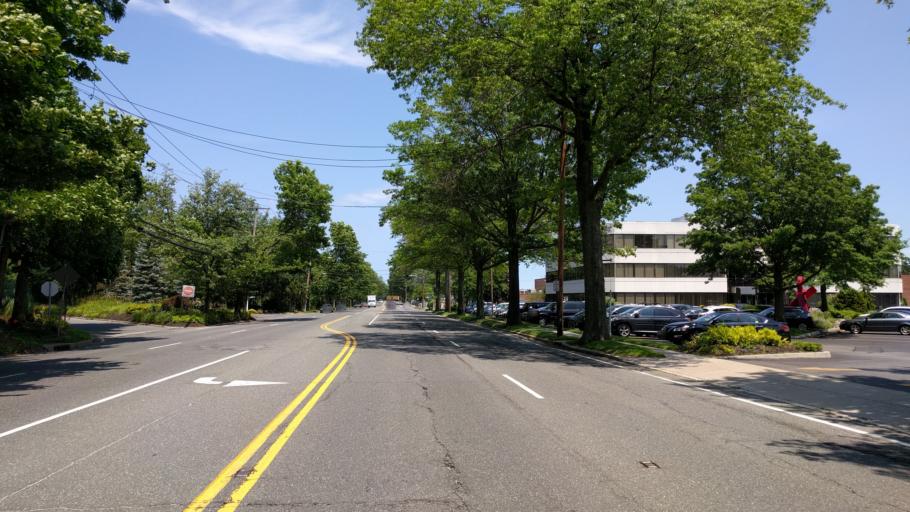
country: US
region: New York
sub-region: Nassau County
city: Syosset
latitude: 40.8135
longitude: -73.5136
